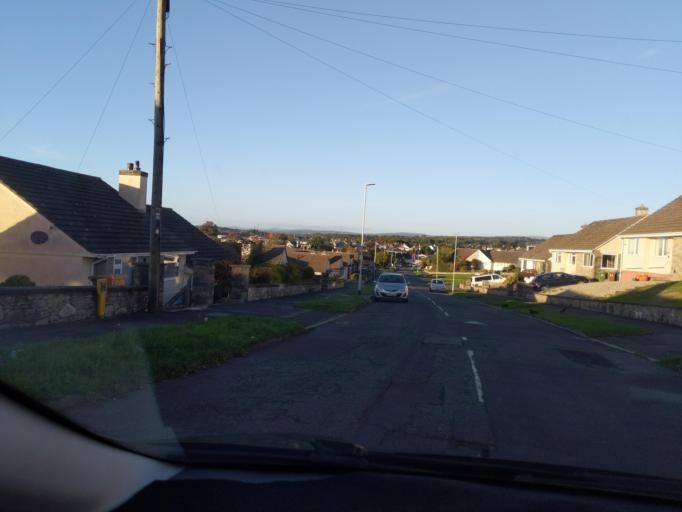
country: GB
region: England
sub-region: Plymouth
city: Plymstock
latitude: 50.3560
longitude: -4.0968
